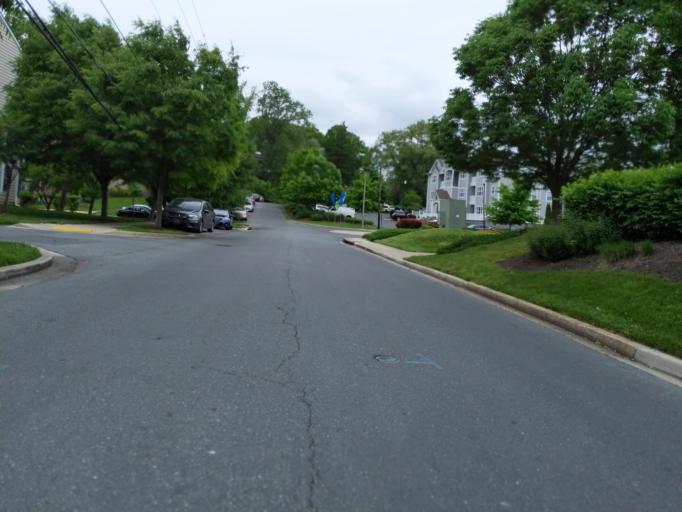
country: US
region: Maryland
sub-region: Montgomery County
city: Wheaton
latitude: 39.0328
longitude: -77.0437
